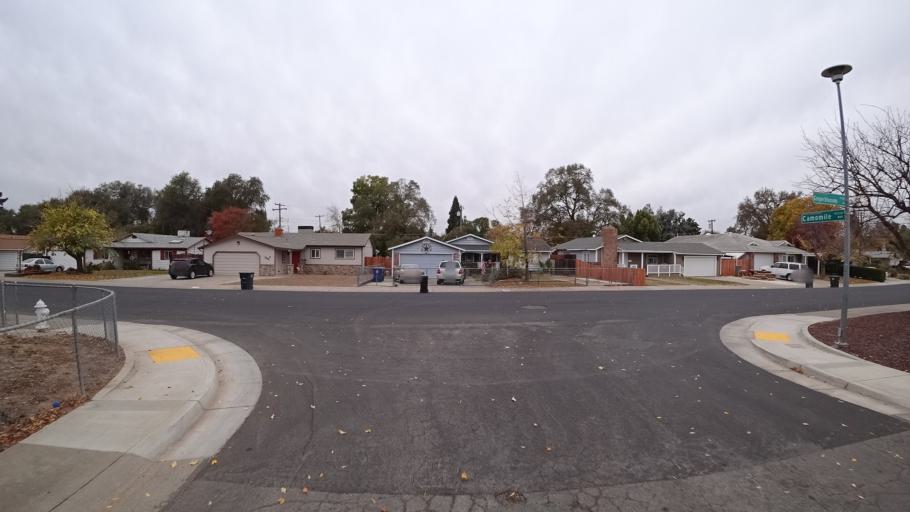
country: US
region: California
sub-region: Sacramento County
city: Citrus Heights
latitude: 38.7056
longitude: -121.3044
